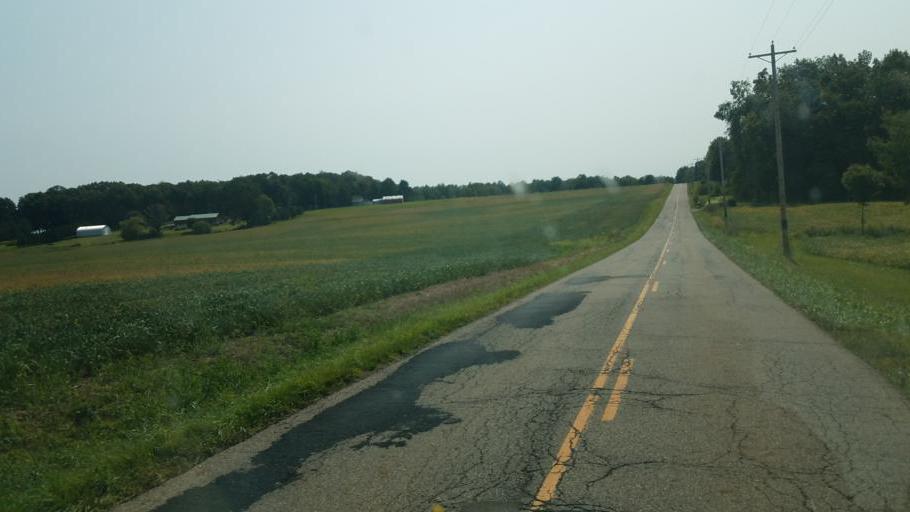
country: US
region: Ohio
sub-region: Knox County
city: Fredericktown
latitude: 40.5017
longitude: -82.4839
